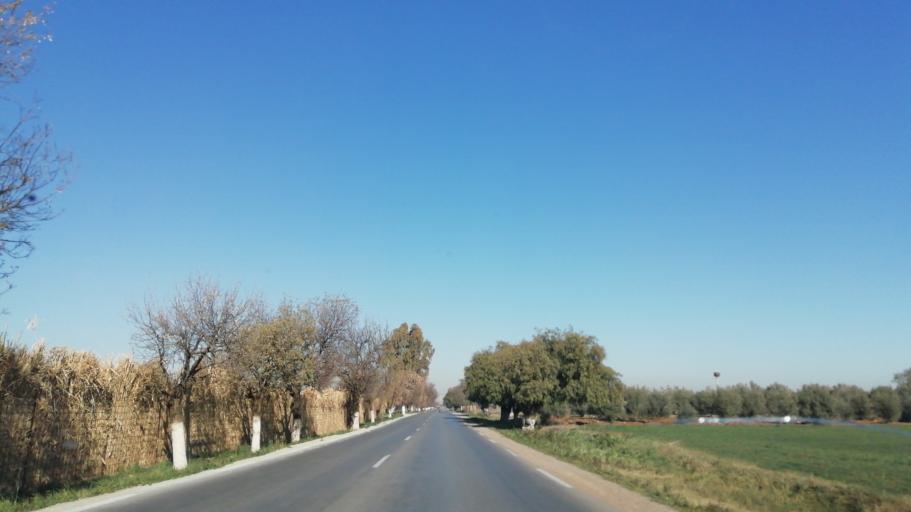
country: DZ
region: Mascara
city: Mascara
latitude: 35.2843
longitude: 0.1280
